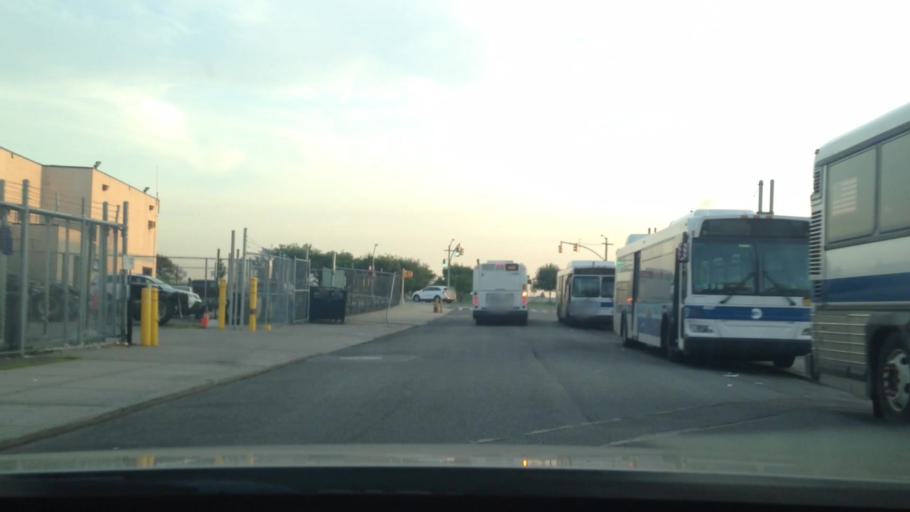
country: US
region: New York
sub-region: Queens County
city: Long Island City
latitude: 40.7661
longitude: -73.8845
